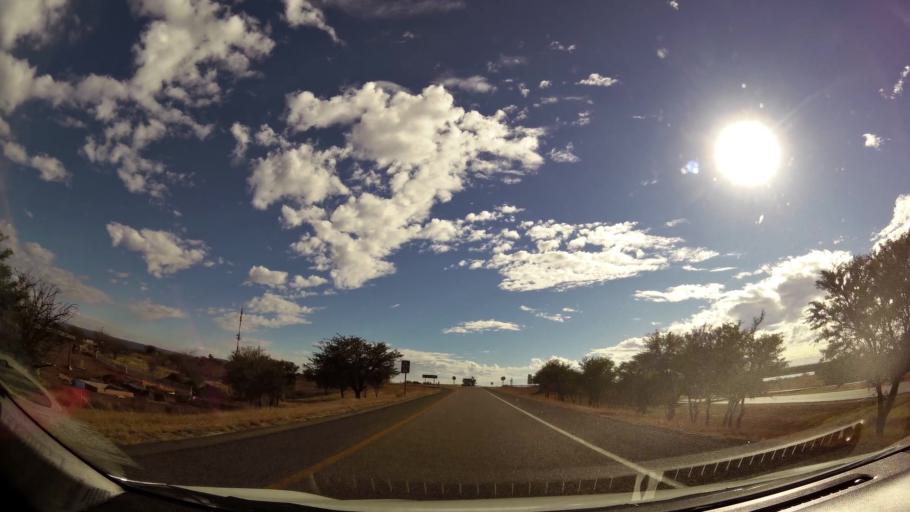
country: ZA
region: Limpopo
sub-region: Waterberg District Municipality
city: Bela-Bela
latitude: -24.9199
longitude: 28.3717
